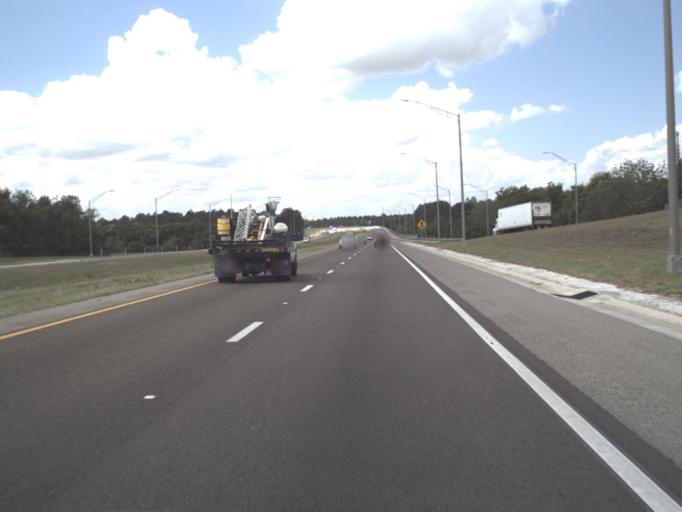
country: US
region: Florida
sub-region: Orange County
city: Paradise Heights
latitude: 28.6009
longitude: -81.5459
